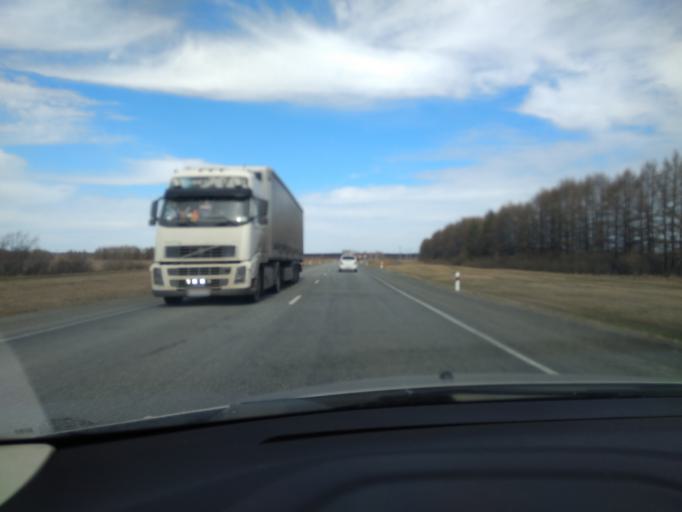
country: RU
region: Sverdlovsk
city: Pyshma
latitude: 57.0400
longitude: 63.4297
